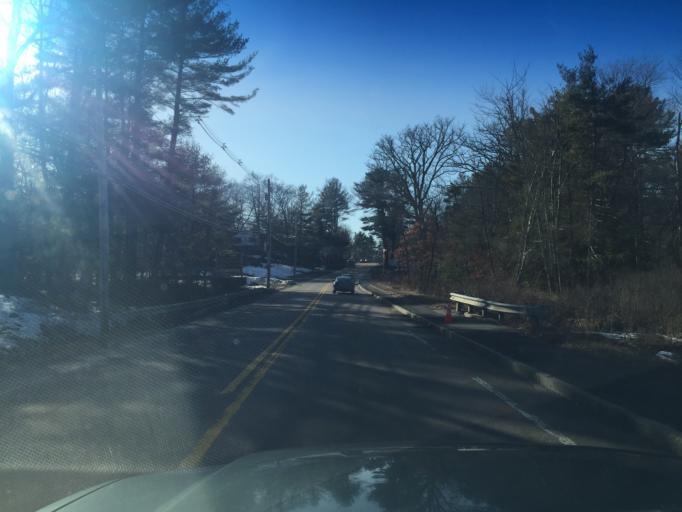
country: US
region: Massachusetts
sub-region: Norfolk County
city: Bellingham
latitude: 42.0870
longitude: -71.4913
